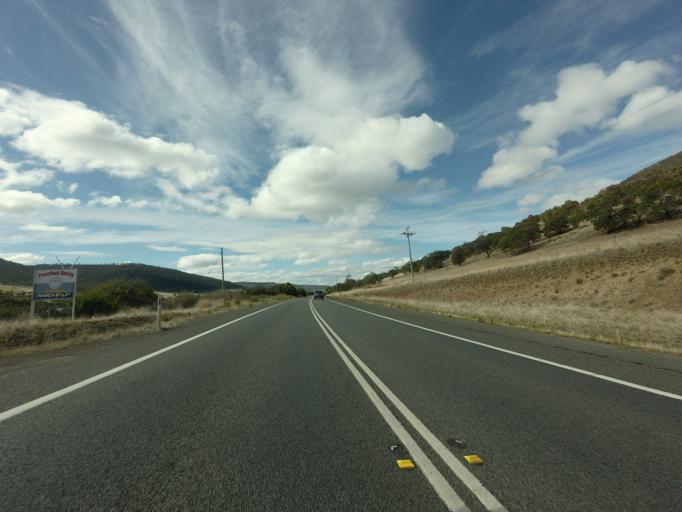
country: AU
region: Tasmania
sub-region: Glenorchy
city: Granton
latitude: -42.7600
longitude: 147.1474
